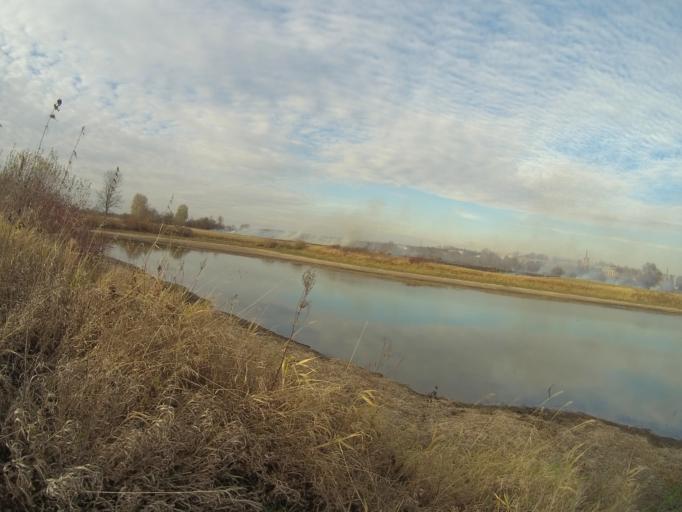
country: RU
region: Vladimir
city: Orgtrud
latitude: 56.1761
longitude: 40.5986
